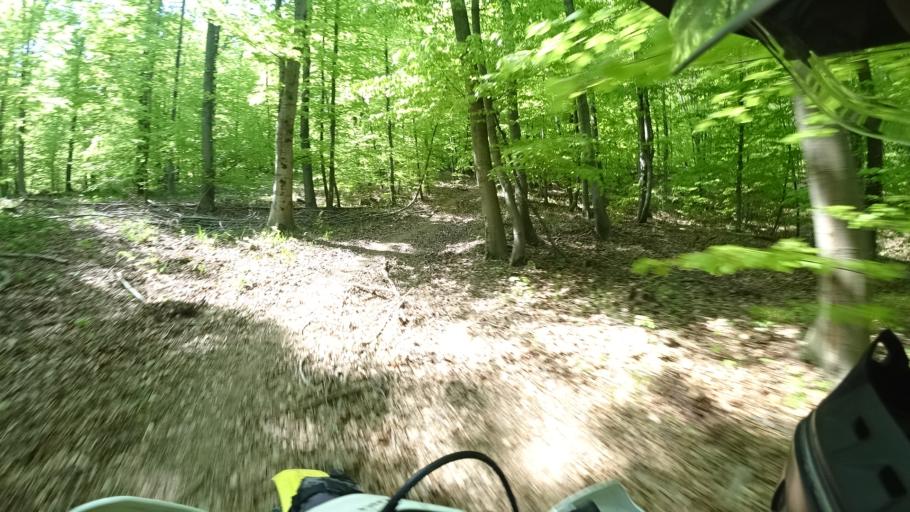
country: HR
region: Grad Zagreb
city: Stenjevec
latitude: 45.8574
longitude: 15.9085
